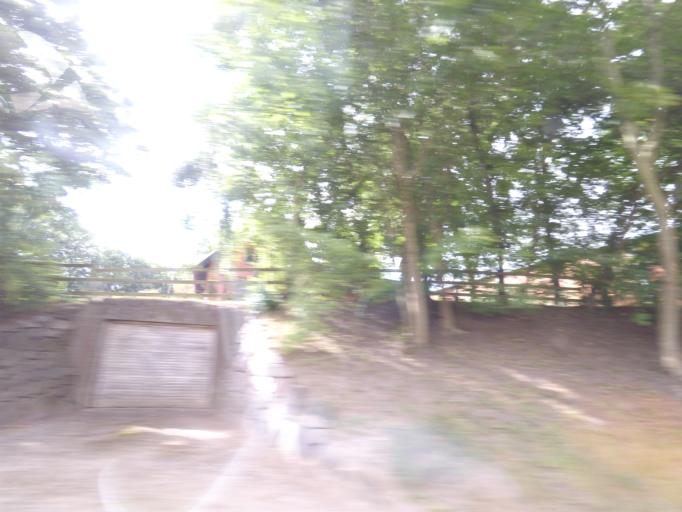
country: DK
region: South Denmark
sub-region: Nordfyns Kommune
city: Sonderso
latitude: 55.4613
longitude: 10.1936
